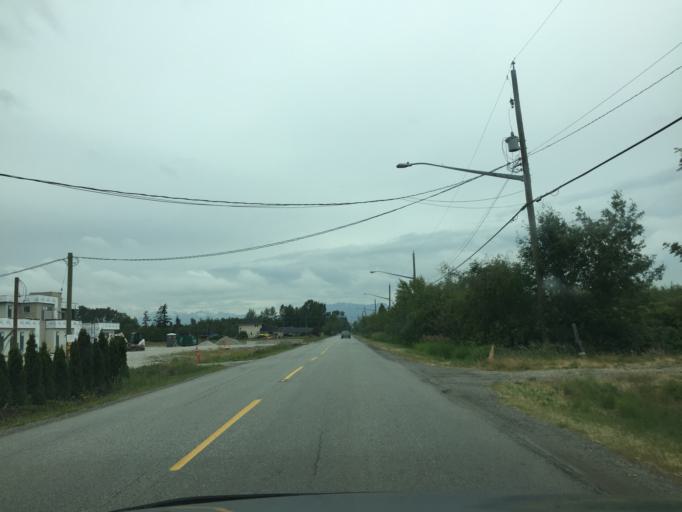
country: CA
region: British Columbia
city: Richmond
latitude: 49.1660
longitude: -123.0804
